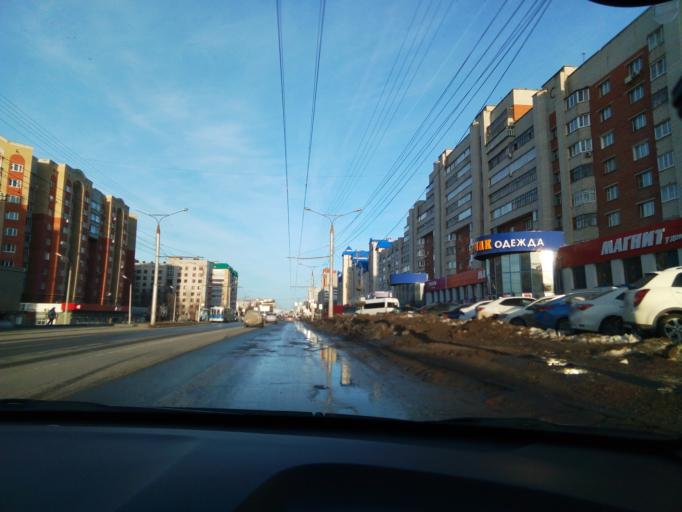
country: RU
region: Chuvashia
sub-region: Cheboksarskiy Rayon
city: Cheboksary
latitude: 56.1487
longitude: 47.1750
